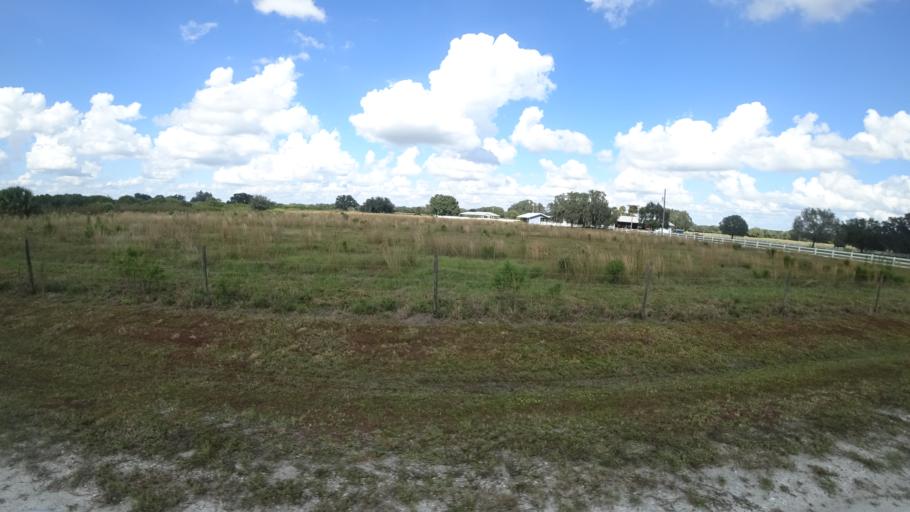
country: US
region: Florida
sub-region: Sarasota County
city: North Port
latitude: 27.2080
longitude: -82.0982
